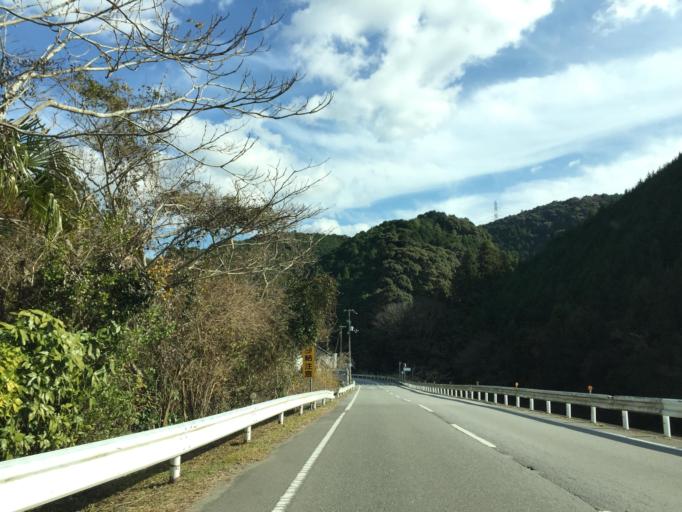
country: JP
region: Wakayama
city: Iwade
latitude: 34.1397
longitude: 135.4143
